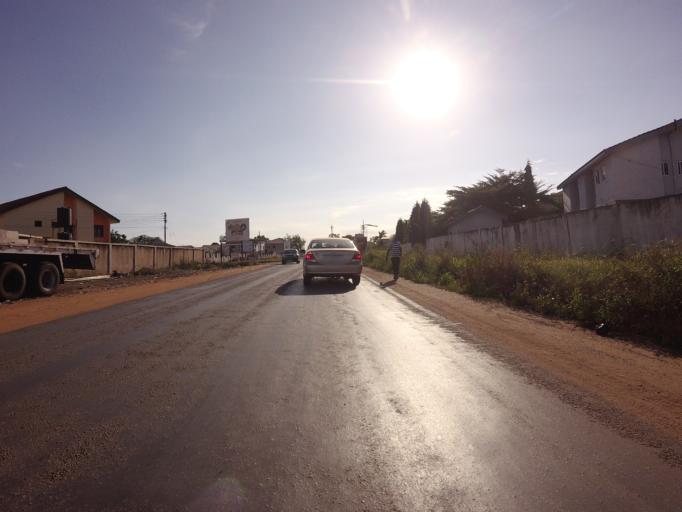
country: GH
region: Greater Accra
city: Nungua
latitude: 5.6493
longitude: -0.0741
